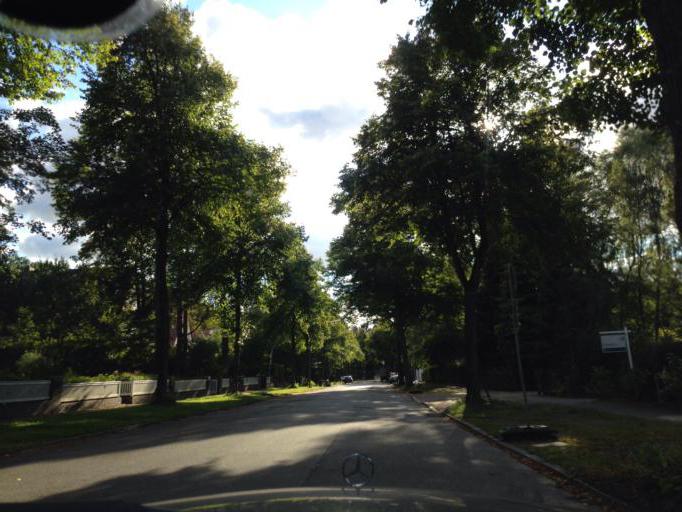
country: DE
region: Hamburg
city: Wandsbek
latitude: 53.5656
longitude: 10.0976
